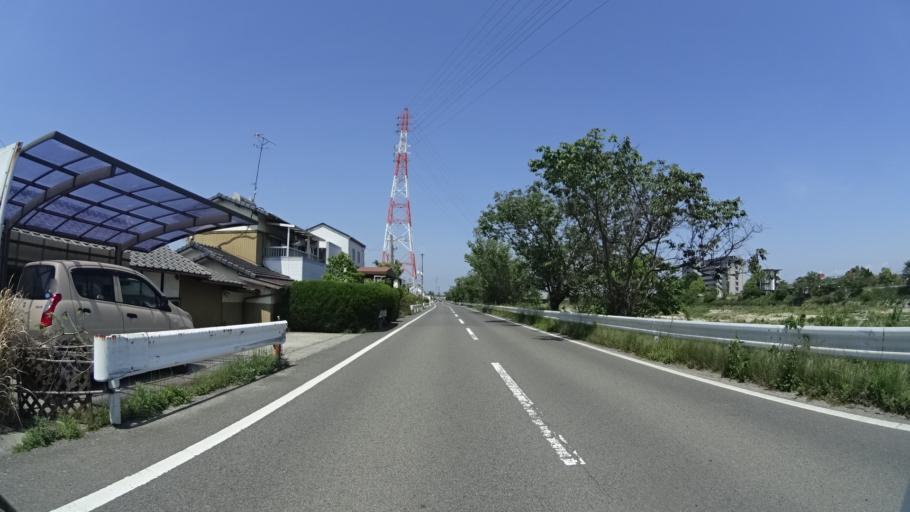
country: JP
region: Ehime
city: Hojo
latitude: 34.0431
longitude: 132.9815
